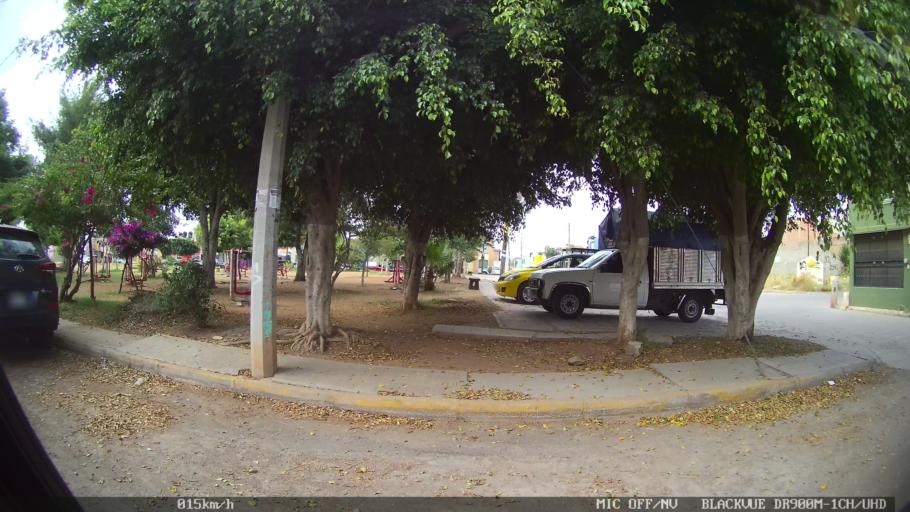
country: MX
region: Jalisco
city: Tonala
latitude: 20.6333
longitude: -103.2352
